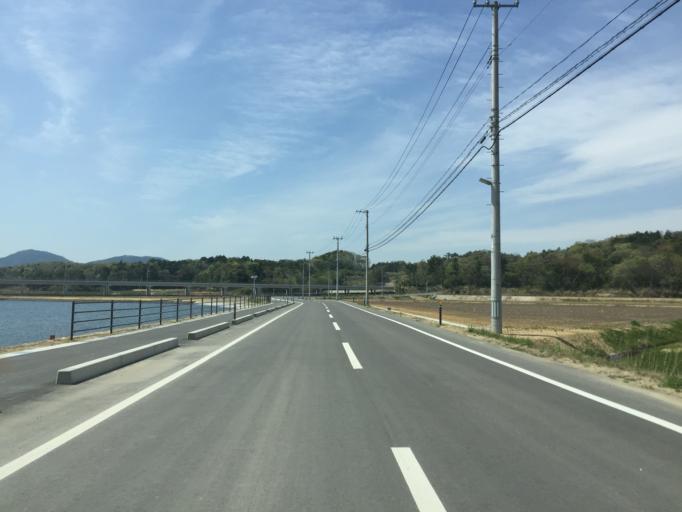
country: JP
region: Miyagi
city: Watari
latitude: 37.9019
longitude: 140.9200
